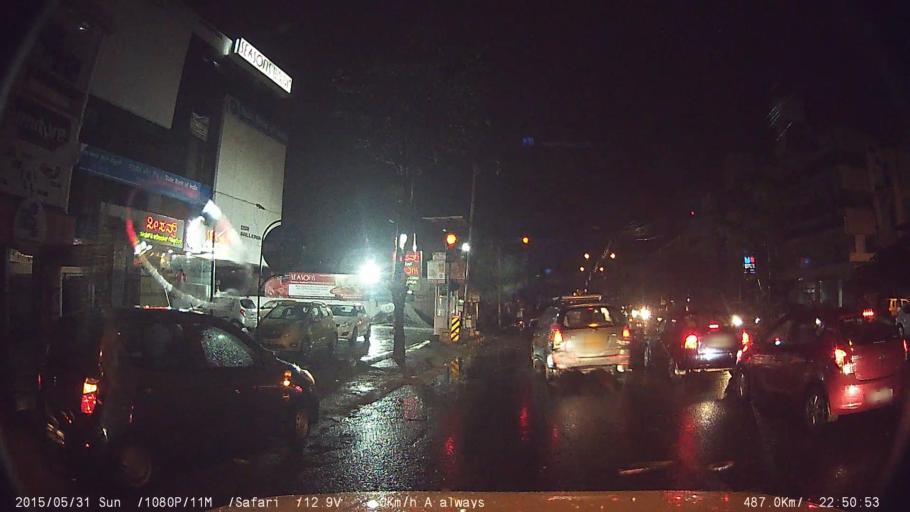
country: IN
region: Karnataka
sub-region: Bangalore Urban
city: Bangalore
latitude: 12.9018
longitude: 77.6011
